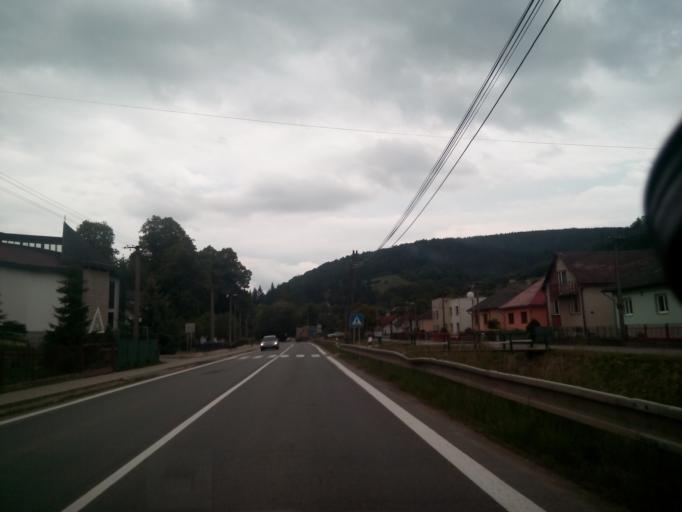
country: SK
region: Presovsky
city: Lipany
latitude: 49.0162
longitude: 20.9692
